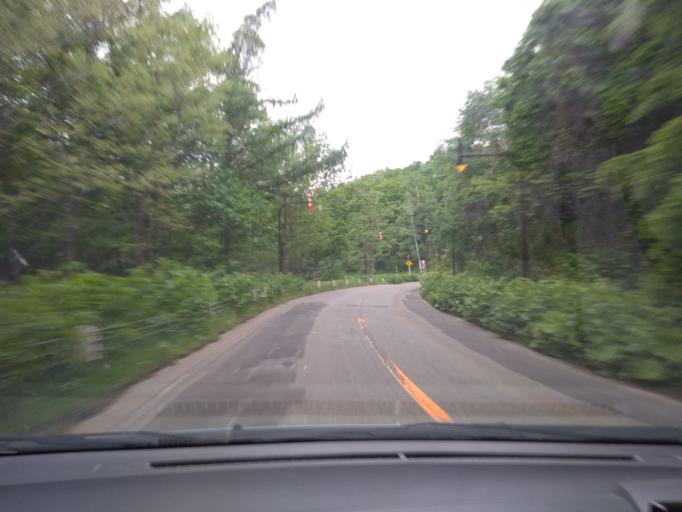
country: JP
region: Hokkaido
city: Shimo-furano
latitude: 43.1383
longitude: 142.4709
